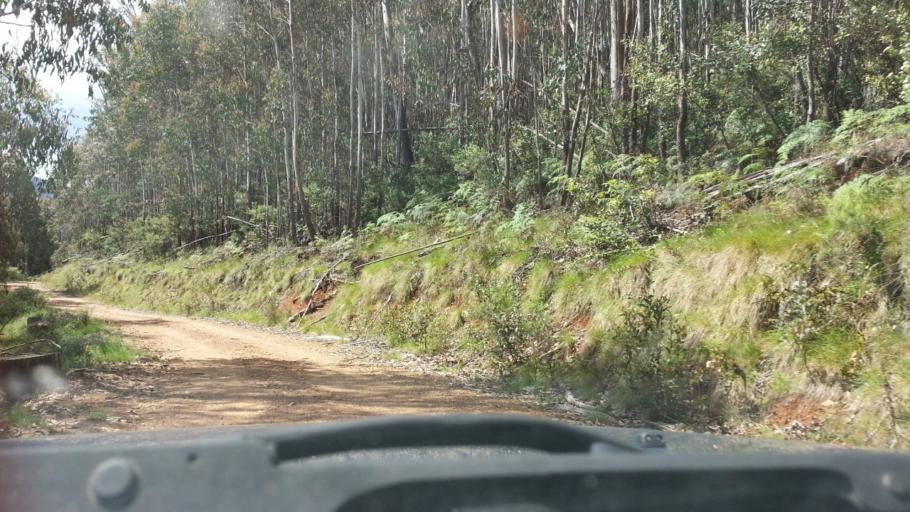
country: AU
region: Victoria
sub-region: Alpine
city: Mount Beauty
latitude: -36.6895
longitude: 147.3034
